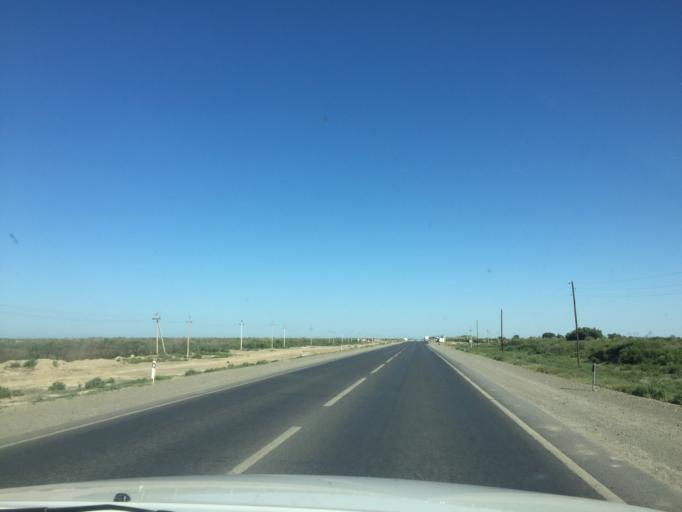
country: KZ
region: Qyzylorda
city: Kyzyl-Orda
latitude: 44.7967
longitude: 65.4526
